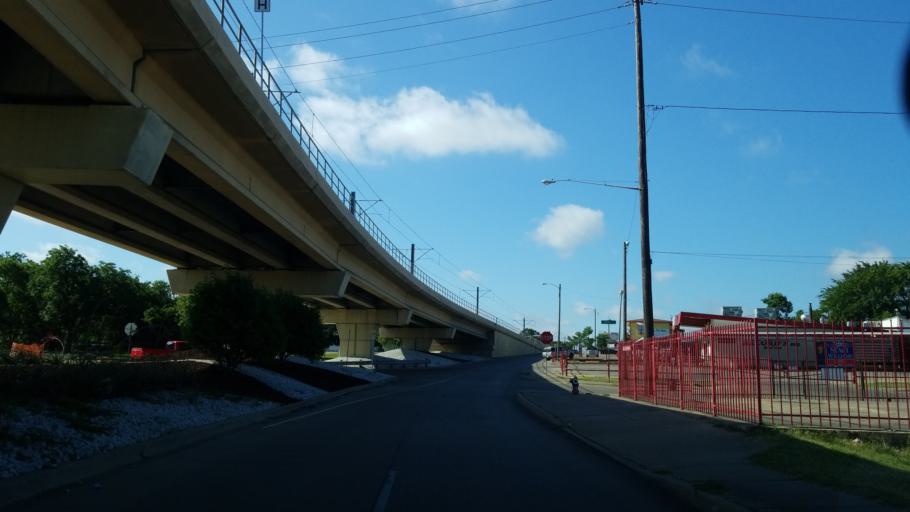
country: US
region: Texas
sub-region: Dallas County
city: Dallas
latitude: 32.7194
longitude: -96.8047
